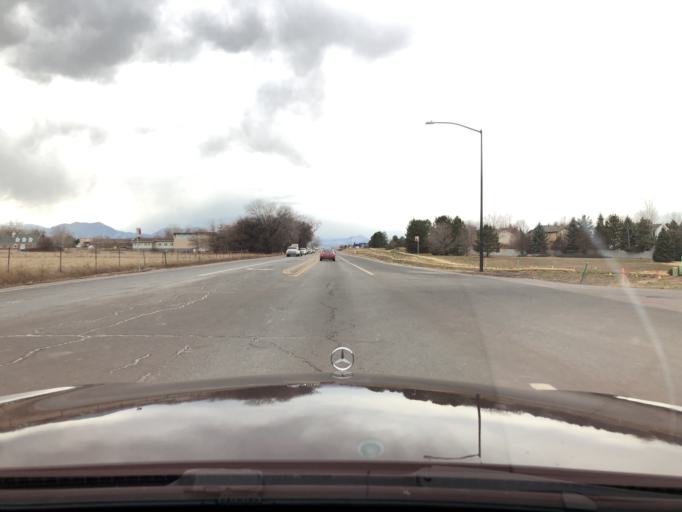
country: US
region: Colorado
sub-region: Boulder County
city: Lafayette
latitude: 40.0147
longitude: -105.1215
